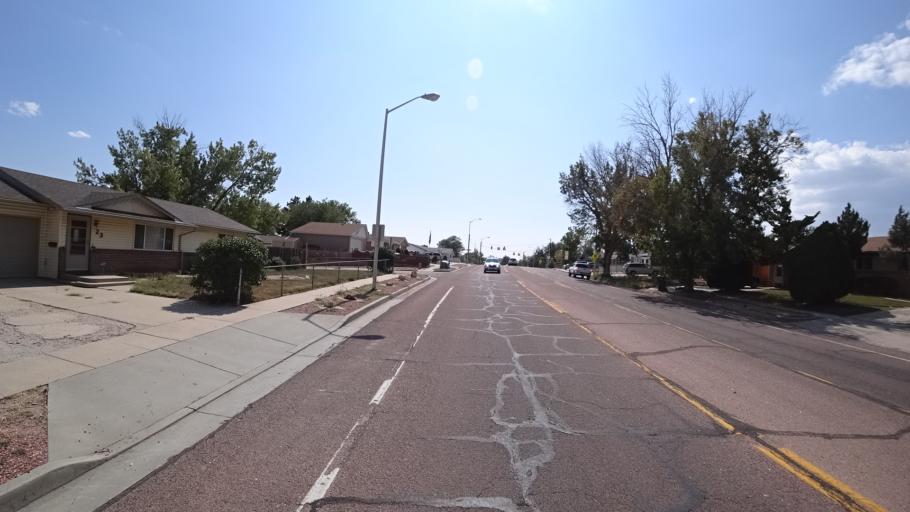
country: US
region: Colorado
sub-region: El Paso County
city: Colorado Springs
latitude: 38.8338
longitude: -104.7663
